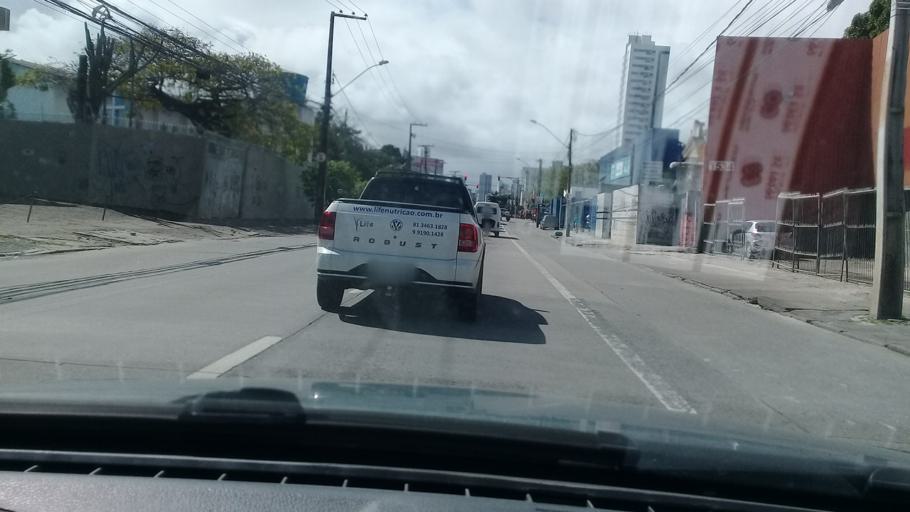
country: BR
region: Pernambuco
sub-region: Recife
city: Recife
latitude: -8.0666
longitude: -34.9083
